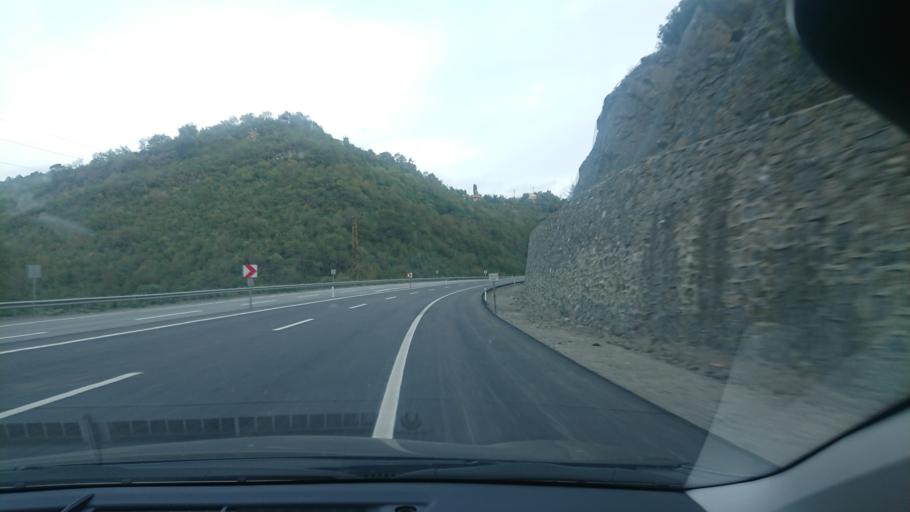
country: TR
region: Zonguldak
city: Beycuma
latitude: 41.3880
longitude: 31.9365
